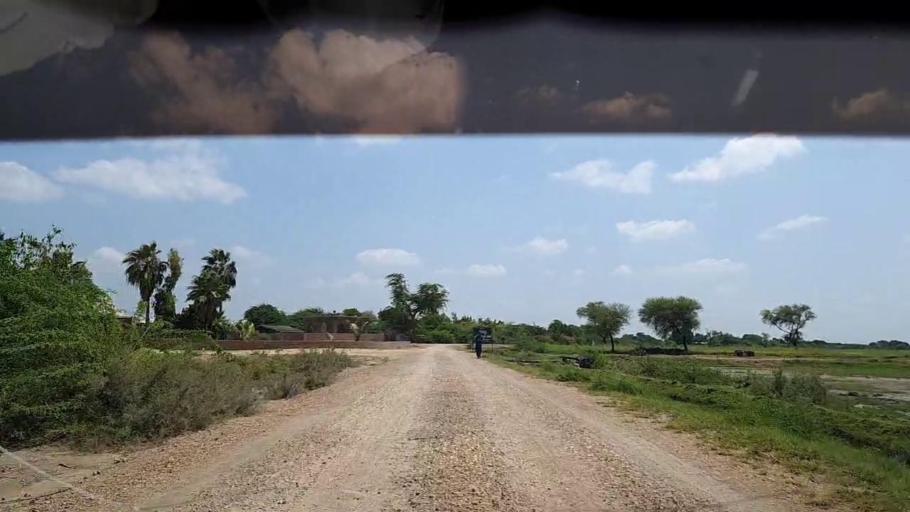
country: PK
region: Sindh
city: Kadhan
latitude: 24.5856
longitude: 68.9594
